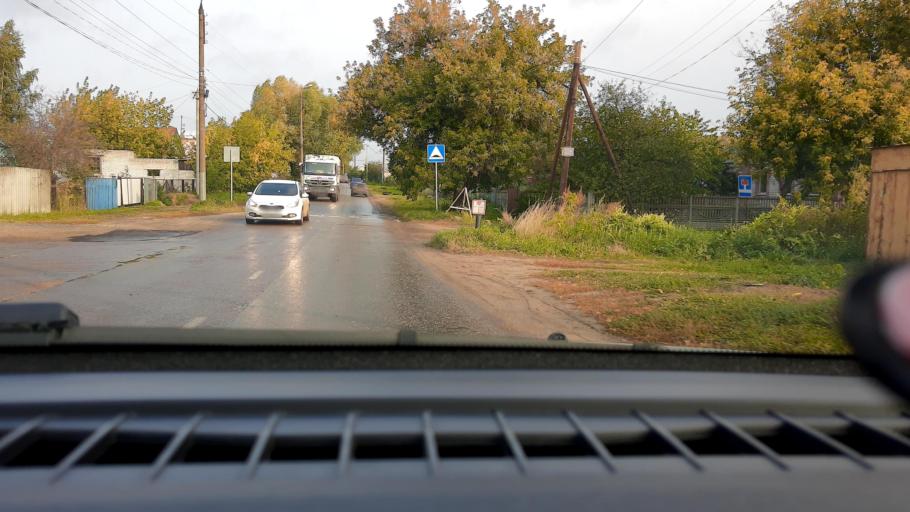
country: RU
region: Nizjnij Novgorod
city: Kstovo
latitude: 56.1880
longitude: 44.1627
